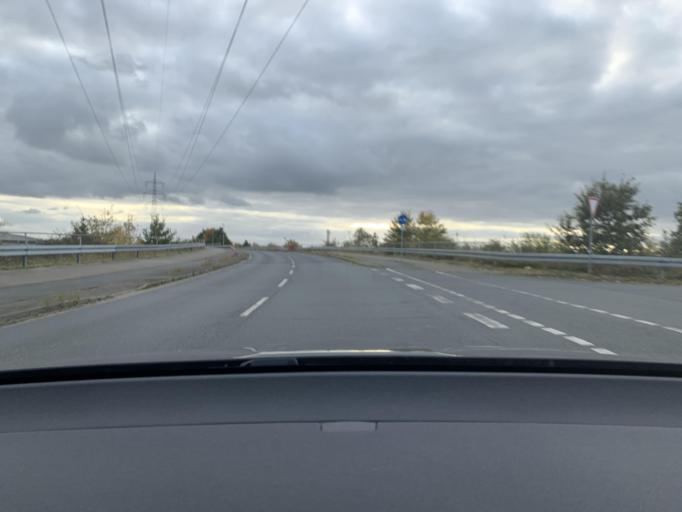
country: DE
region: Lower Saxony
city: Vordorf
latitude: 52.3197
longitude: 10.5014
